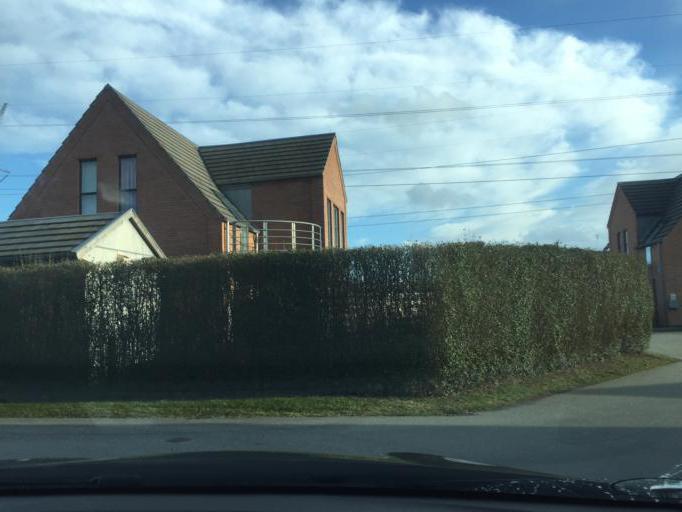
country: DK
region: South Denmark
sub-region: Odense Kommune
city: Neder Holluf
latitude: 55.3555
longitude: 10.4713
